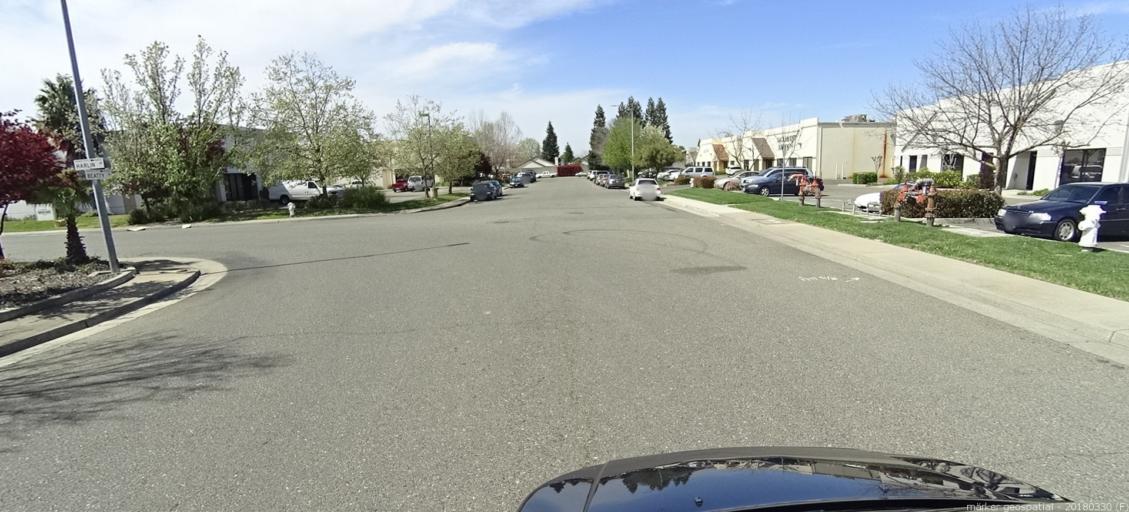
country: US
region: California
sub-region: Sacramento County
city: Rosemont
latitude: 38.5391
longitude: -121.3564
